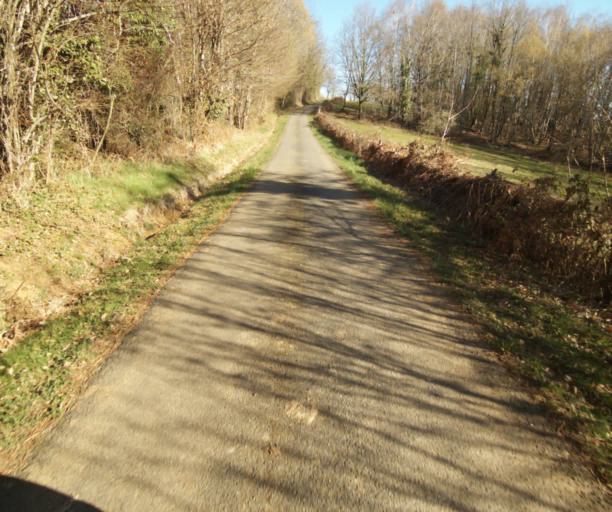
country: FR
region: Limousin
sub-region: Departement de la Correze
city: Chamboulive
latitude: 45.4164
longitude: 1.6834
